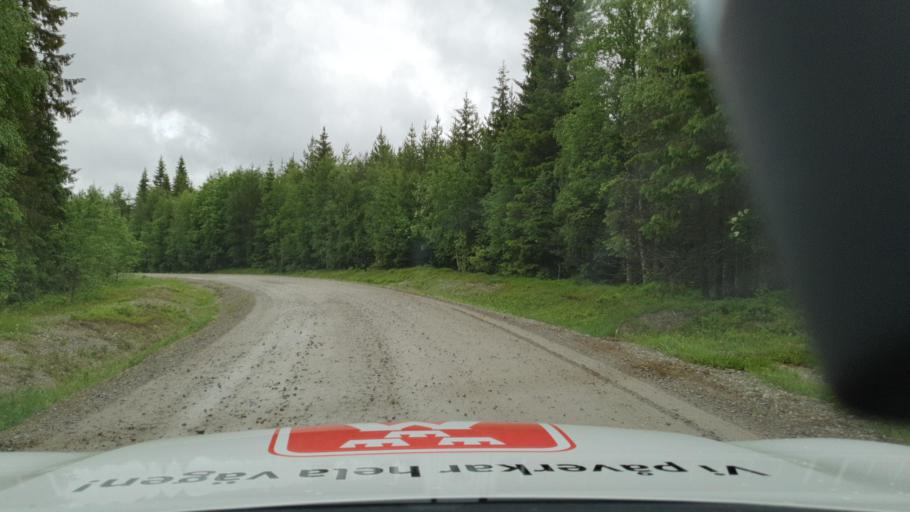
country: SE
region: Vaesterbotten
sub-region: Dorotea Kommun
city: Dorotea
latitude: 64.0276
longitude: 16.7883
